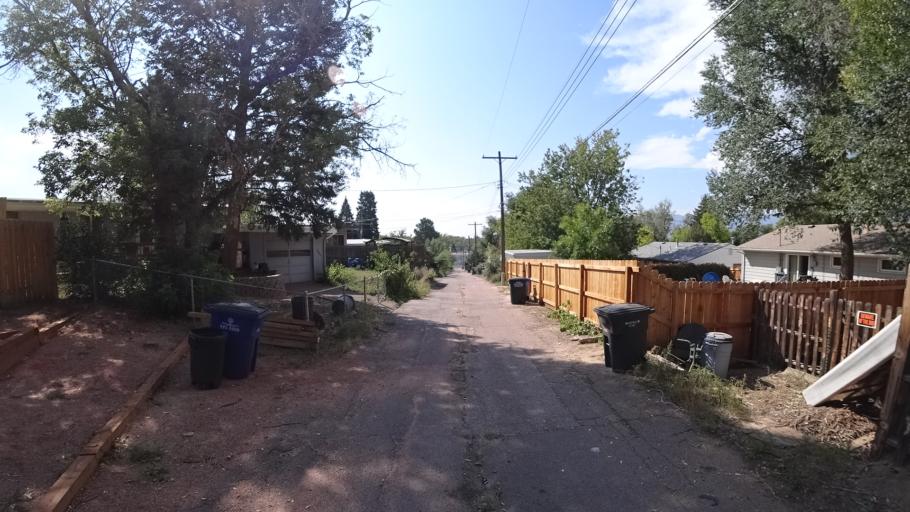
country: US
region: Colorado
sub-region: El Paso County
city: Colorado Springs
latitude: 38.8613
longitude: -104.7731
